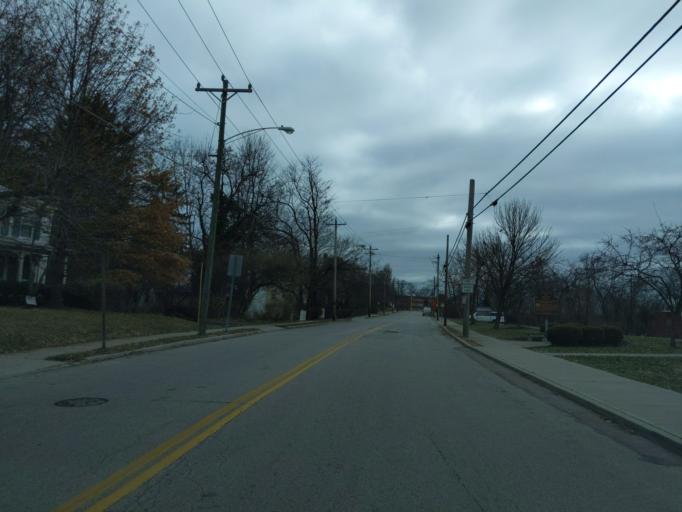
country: US
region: Ohio
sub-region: Hamilton County
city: North College Hill
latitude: 39.1924
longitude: -84.5482
